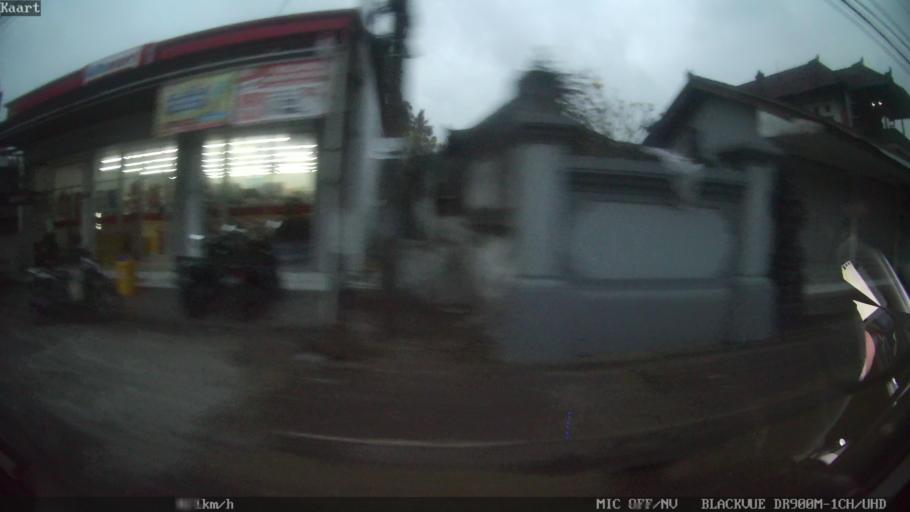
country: ID
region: Bali
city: Banjar Mambalkajanan
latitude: -8.5620
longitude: 115.2204
